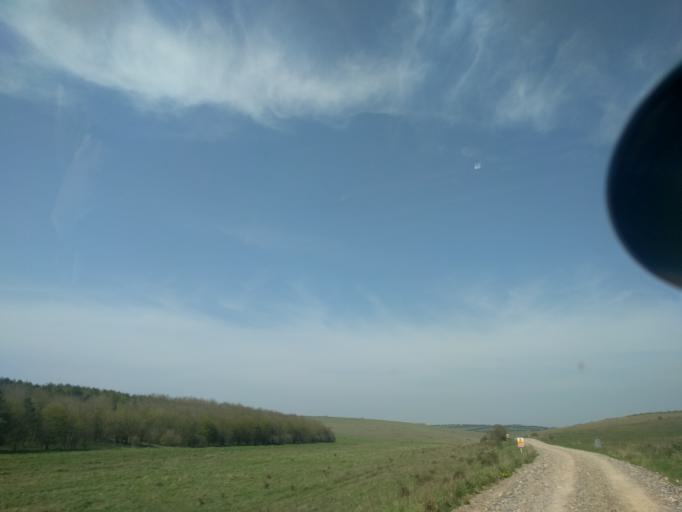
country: GB
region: England
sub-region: Wiltshire
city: Edington
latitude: 51.2369
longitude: -2.0909
